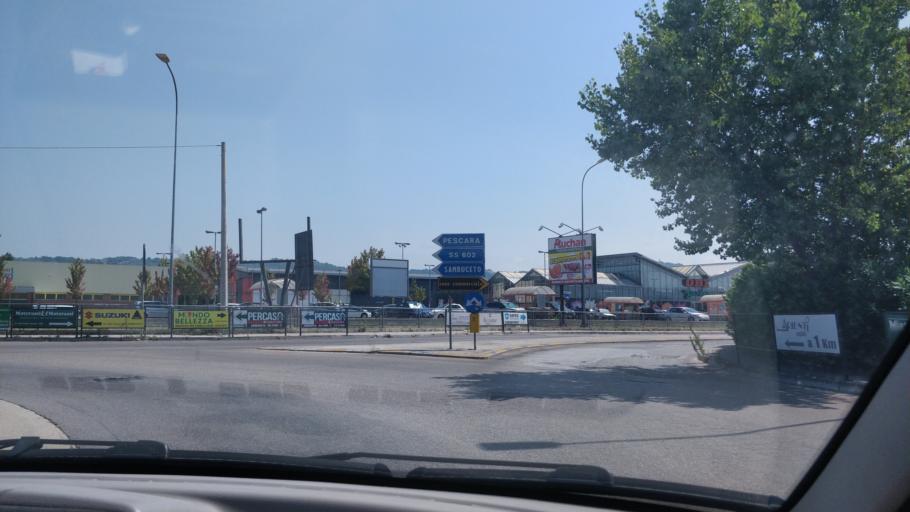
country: IT
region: Abruzzo
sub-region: Provincia di Pescara
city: Santa Teresa
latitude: 42.4159
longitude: 14.1707
